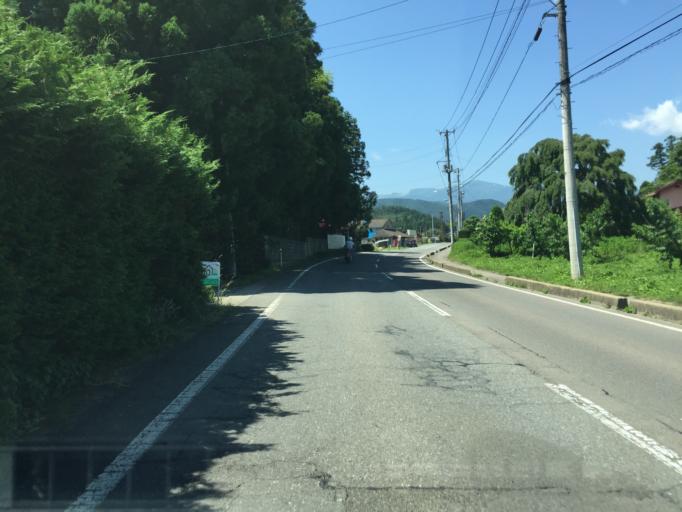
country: JP
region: Fukushima
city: Fukushima-shi
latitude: 37.7210
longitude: 140.4009
